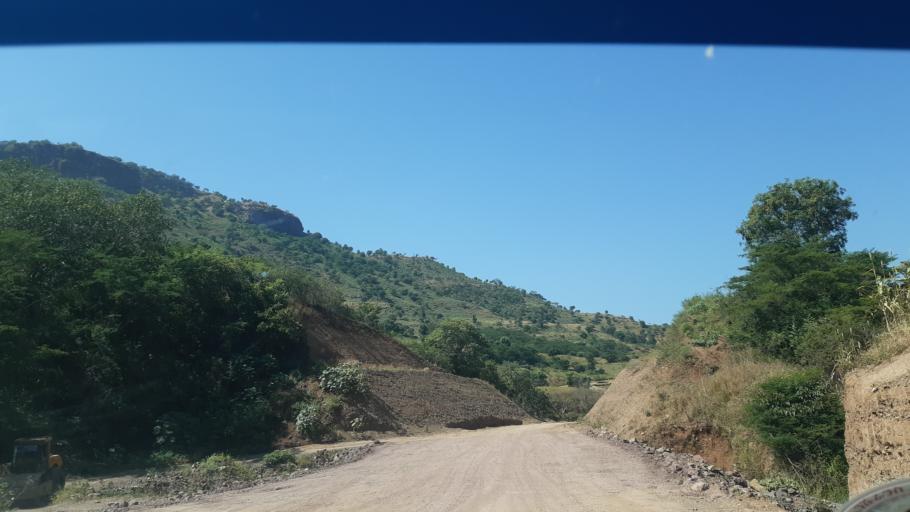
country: ET
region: Amhara
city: Dabat
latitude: 13.1930
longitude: 37.5741
